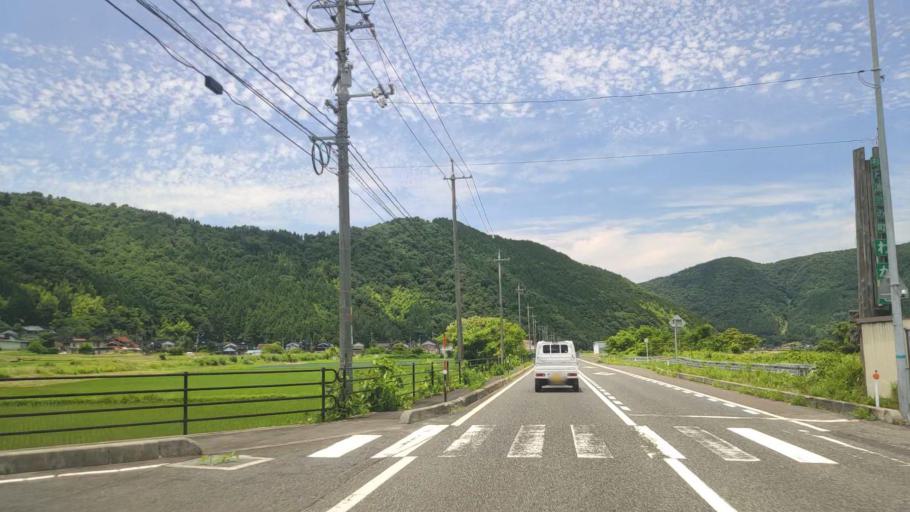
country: JP
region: Tottori
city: Tottori
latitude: 35.3543
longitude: 134.3840
